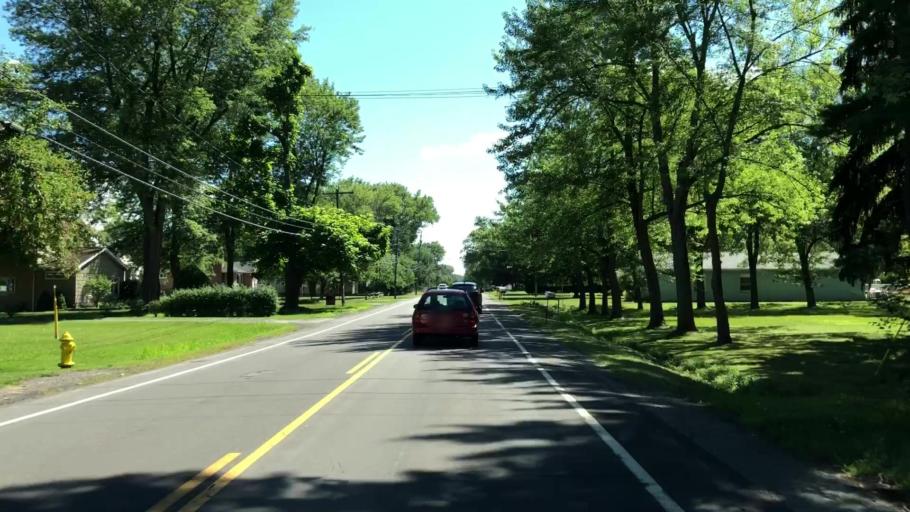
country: US
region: New York
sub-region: Erie County
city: Cheektowaga
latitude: 42.8509
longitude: -78.7325
